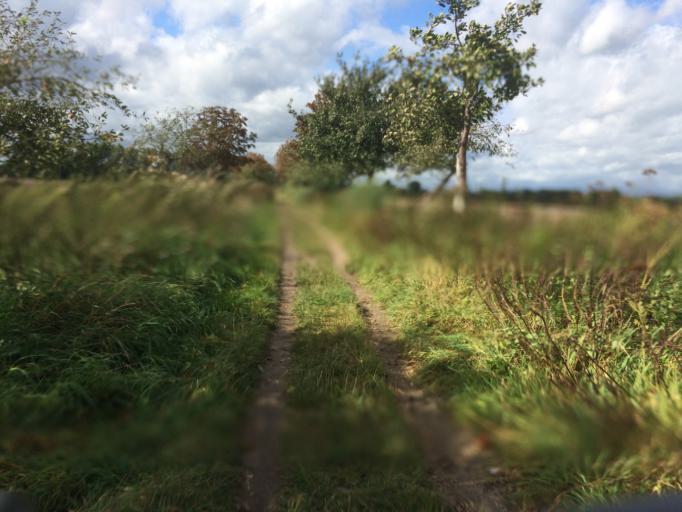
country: DE
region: Berlin
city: Blankenburg
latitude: 52.5837
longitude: 13.4569
